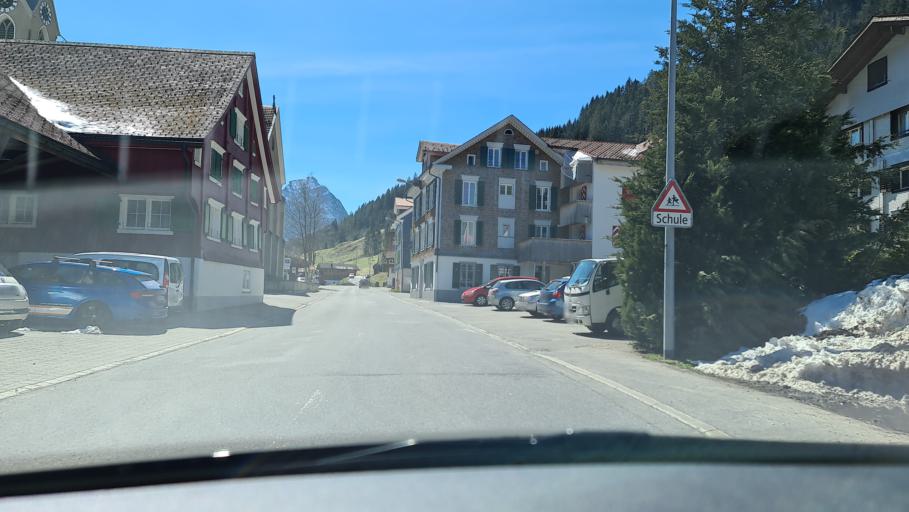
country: CH
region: Schwyz
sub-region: Bezirk Schwyz
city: Rothenthurm
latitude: 47.0715
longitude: 8.7164
